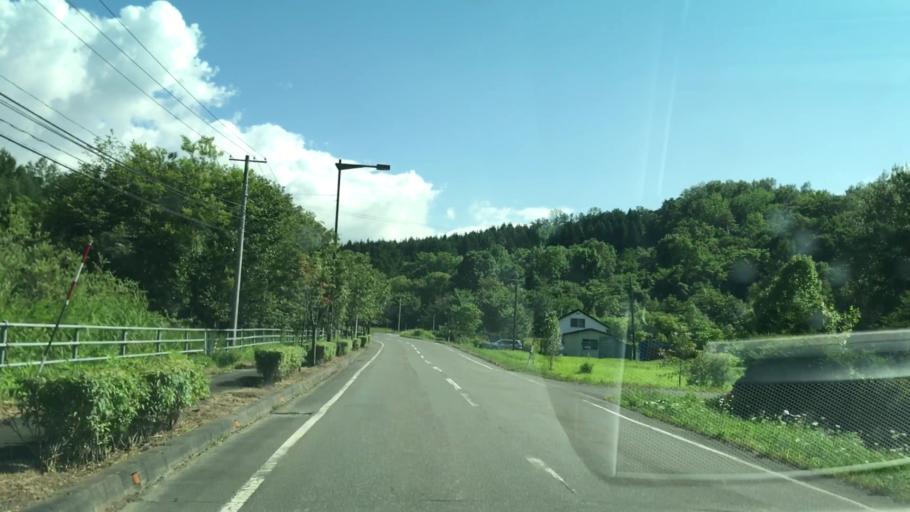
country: JP
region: Hokkaido
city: Shimo-furano
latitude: 42.8659
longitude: 142.4399
